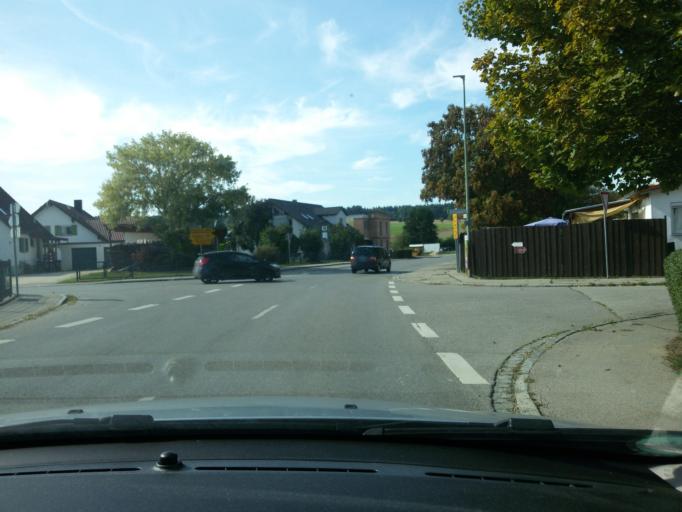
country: DE
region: Bavaria
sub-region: Swabia
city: Mickhausen
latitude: 48.2443
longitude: 10.6401
